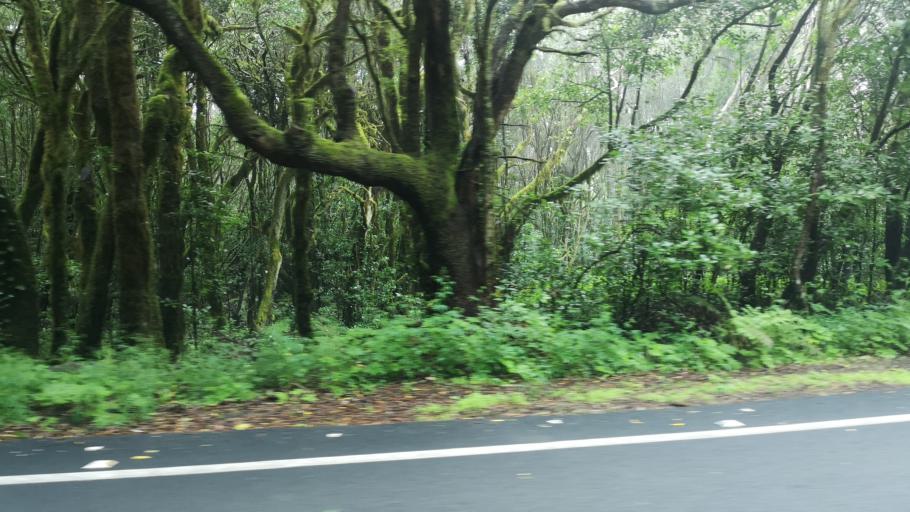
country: ES
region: Canary Islands
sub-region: Provincia de Santa Cruz de Tenerife
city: Vallehermosa
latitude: 28.1547
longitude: -17.2994
